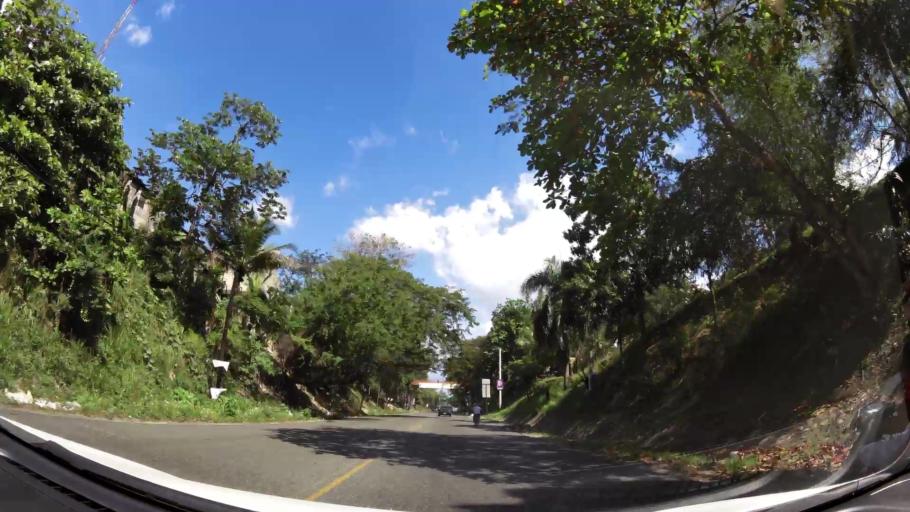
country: DO
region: San Cristobal
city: San Cristobal
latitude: 18.4292
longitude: -70.0864
